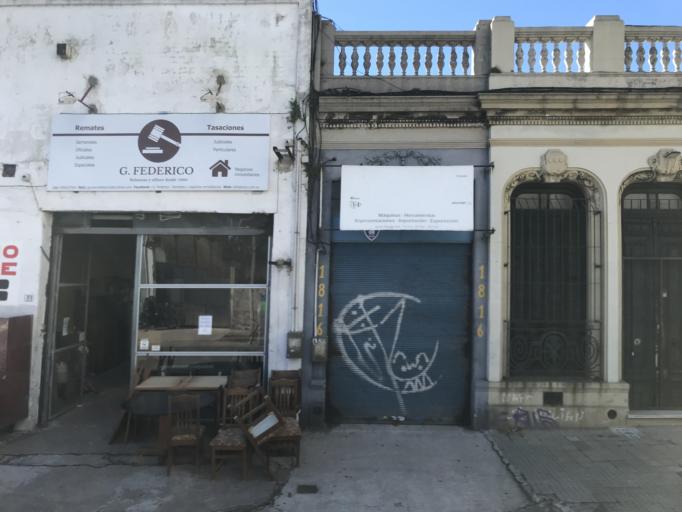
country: UY
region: Montevideo
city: Montevideo
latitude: -34.8964
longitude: -56.1792
